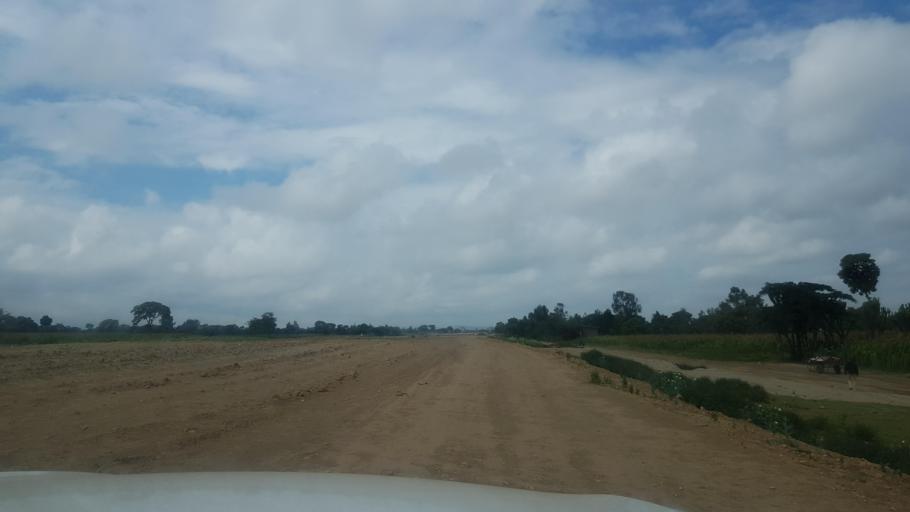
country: ET
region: Oromiya
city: Shashemene
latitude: 7.2659
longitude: 38.5972
